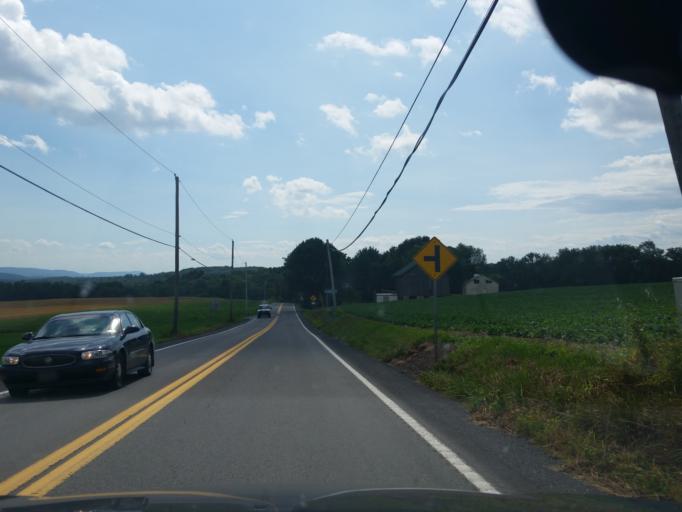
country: US
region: Pennsylvania
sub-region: Dauphin County
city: Elizabethville
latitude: 40.5152
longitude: -76.8510
